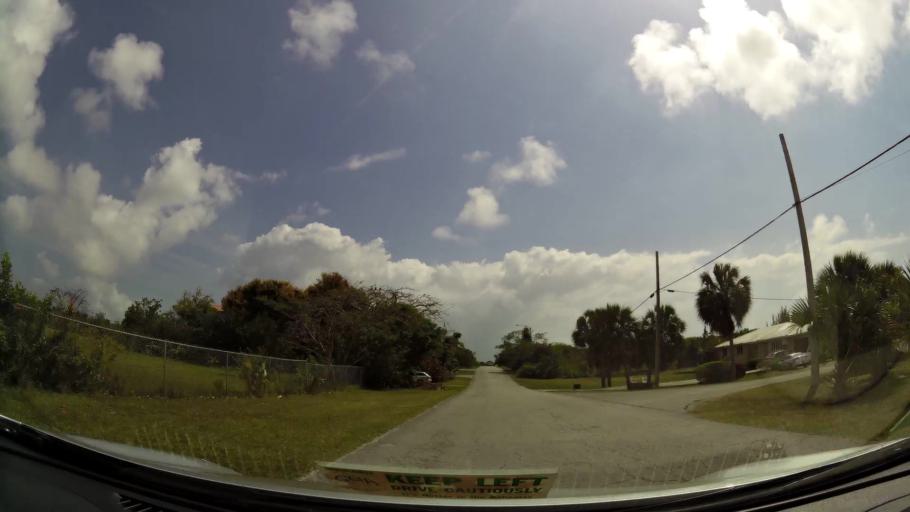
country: BS
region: Freeport
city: Freeport
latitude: 26.5141
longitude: -78.7144
